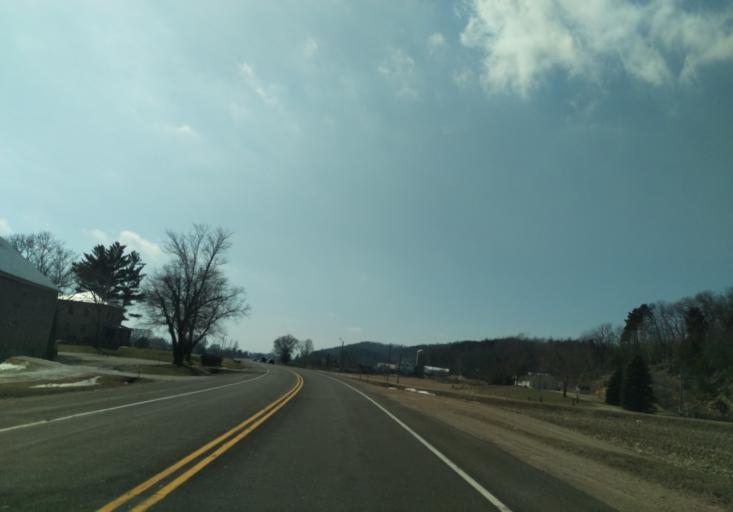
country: US
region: Wisconsin
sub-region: La Crosse County
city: La Crosse
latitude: 43.7646
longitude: -91.1783
